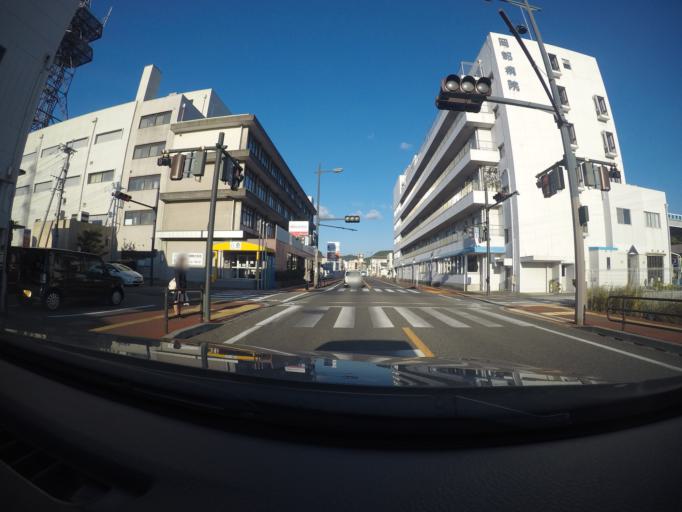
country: JP
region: Kumamoto
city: Minamata
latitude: 32.2074
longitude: 130.3978
